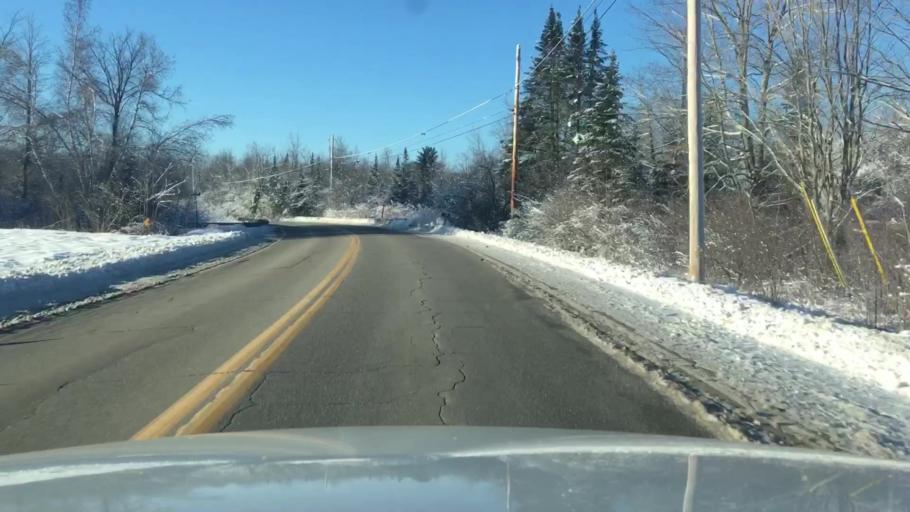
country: US
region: Maine
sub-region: Kennebec County
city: Belgrade
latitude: 44.4089
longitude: -69.8616
